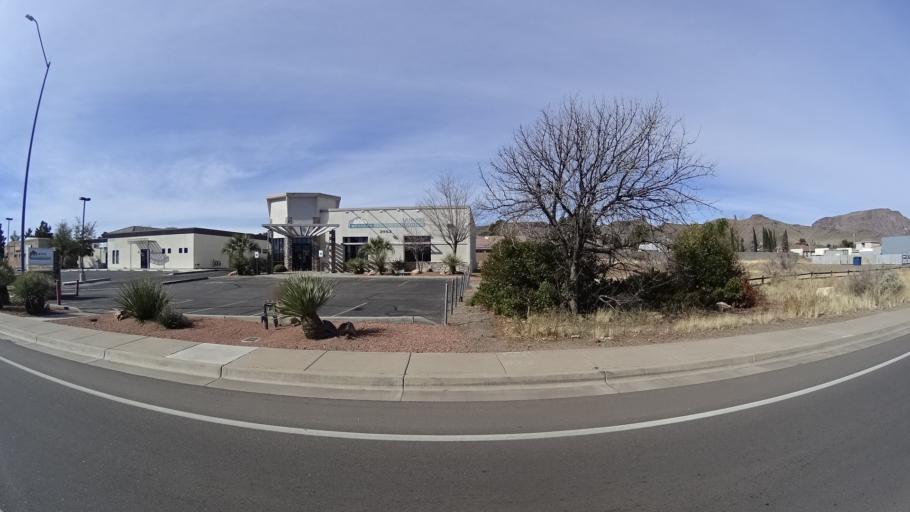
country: US
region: Arizona
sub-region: Mohave County
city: New Kingman-Butler
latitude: 35.2376
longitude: -114.0376
